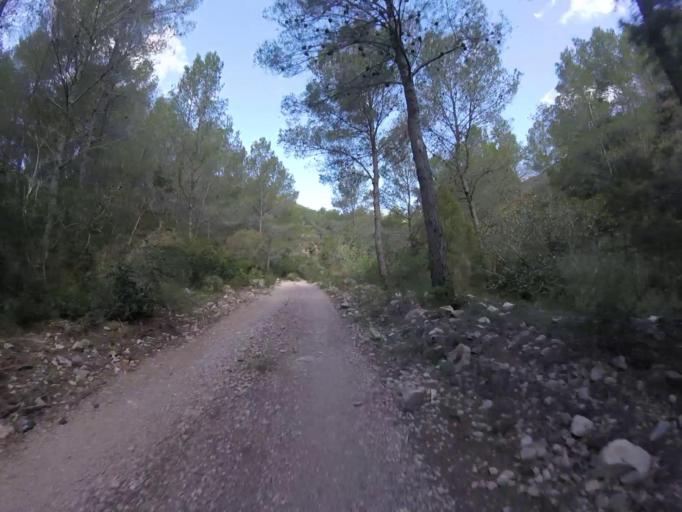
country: ES
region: Valencia
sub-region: Provincia de Castello
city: Alcoceber
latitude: 40.2957
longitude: 0.3144
